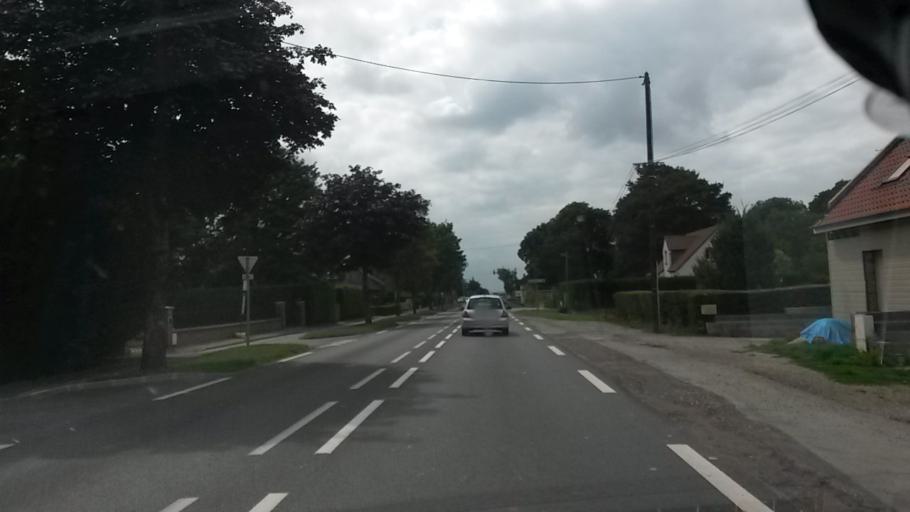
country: FR
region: Picardie
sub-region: Departement de la Somme
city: Camon
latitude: 49.9218
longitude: 2.3710
